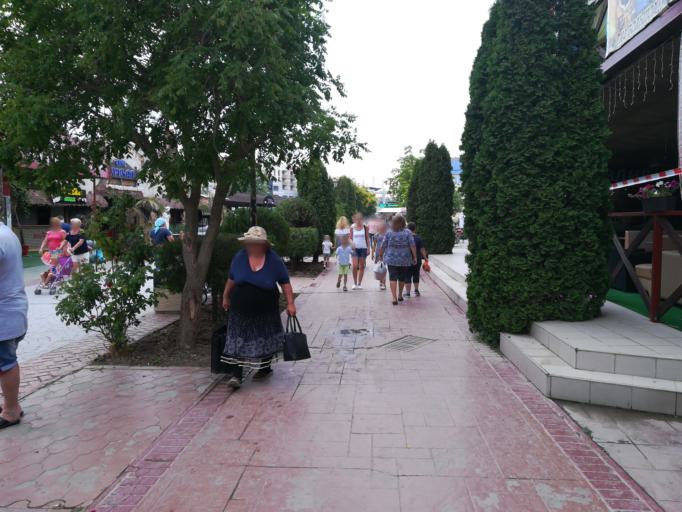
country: RU
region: Krasnodarskiy
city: Vityazevo
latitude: 44.9877
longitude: 37.2560
